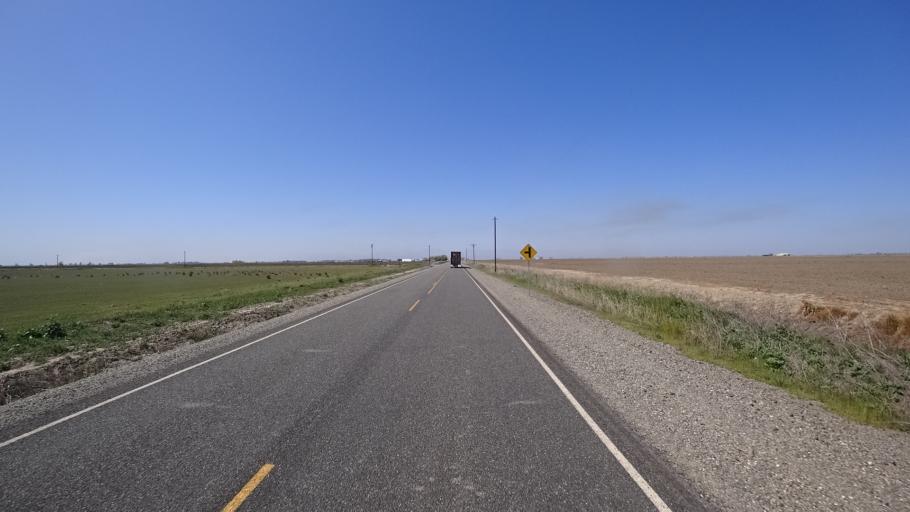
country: US
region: California
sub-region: Glenn County
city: Willows
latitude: 39.4578
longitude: -122.0618
